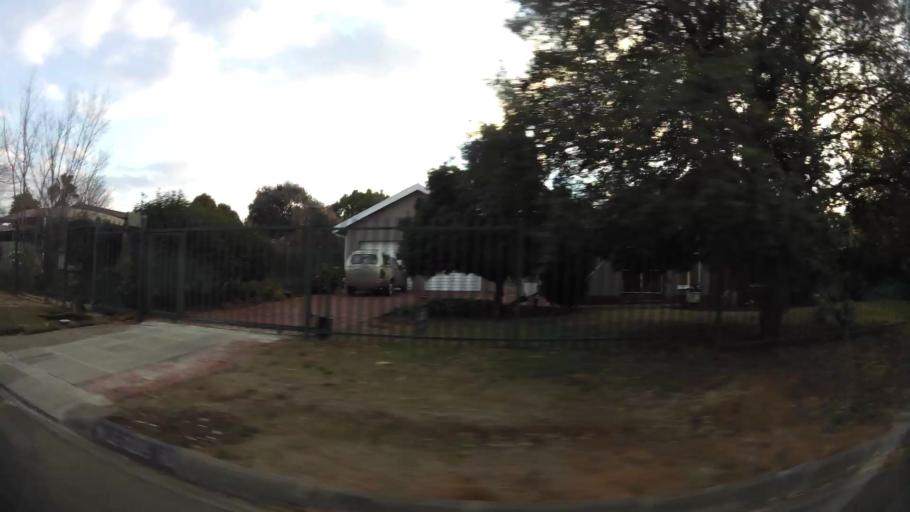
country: ZA
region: Orange Free State
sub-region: Mangaung Metropolitan Municipality
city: Bloemfontein
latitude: -29.1356
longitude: 26.1755
